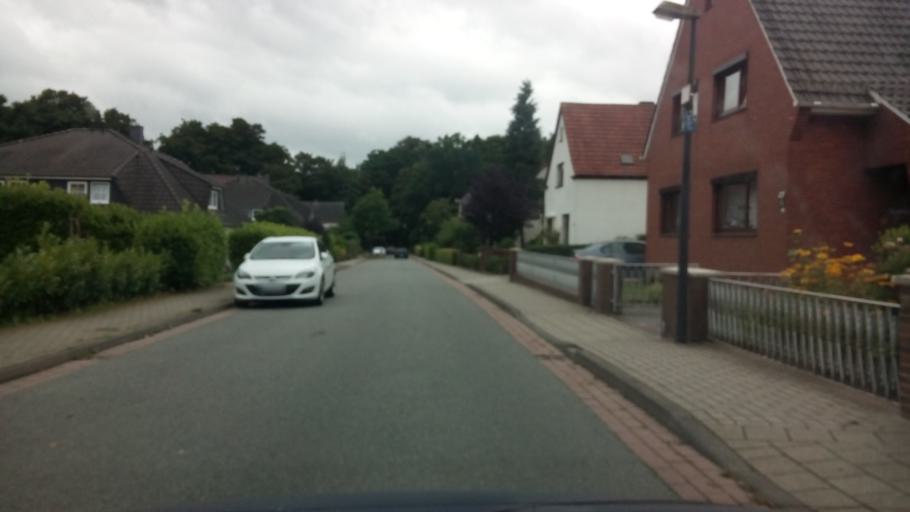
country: DE
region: Lower Saxony
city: Lemwerder
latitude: 53.1903
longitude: 8.6145
